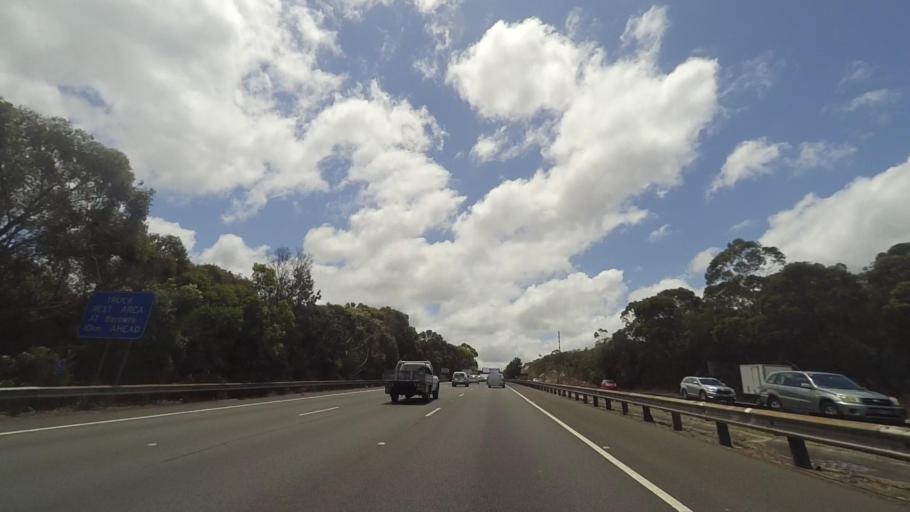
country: AU
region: New South Wales
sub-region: Hornsby Shire
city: Mount Colah
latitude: -33.6818
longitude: 151.1204
